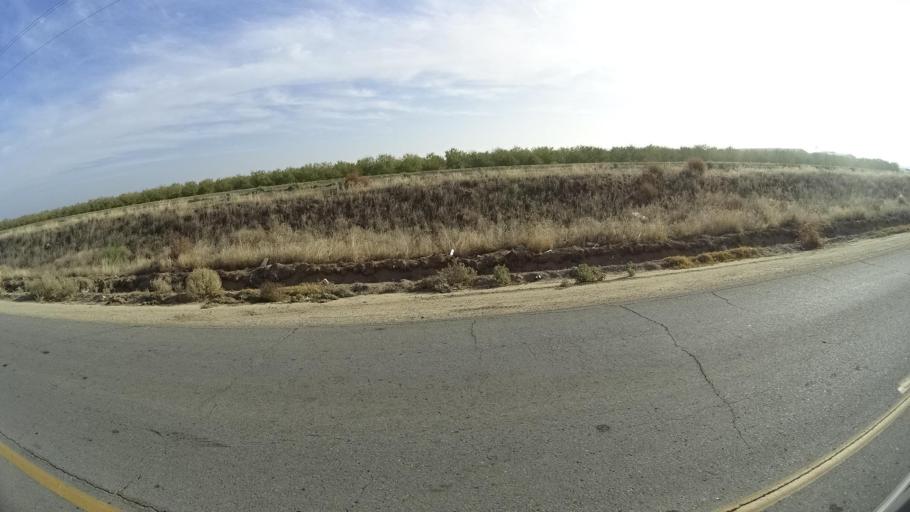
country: US
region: California
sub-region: Kern County
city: McFarland
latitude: 35.6472
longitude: -119.2046
